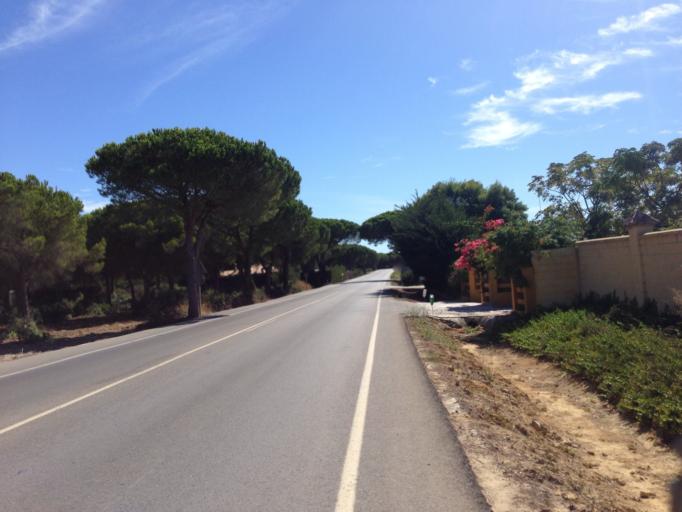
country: ES
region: Andalusia
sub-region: Provincia de Cadiz
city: Conil de la Frontera
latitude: 36.3155
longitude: -6.1043
